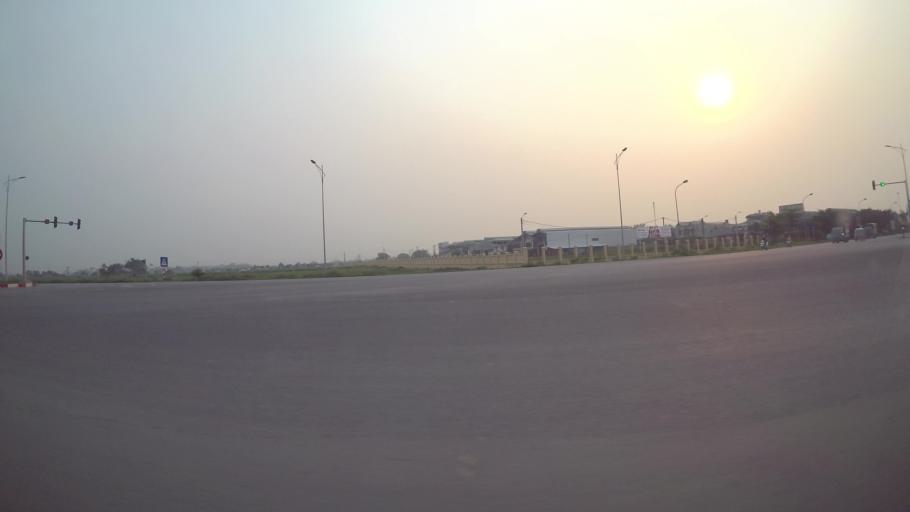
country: VN
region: Ha Noi
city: Kim Bai
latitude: 20.8728
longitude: 105.8033
